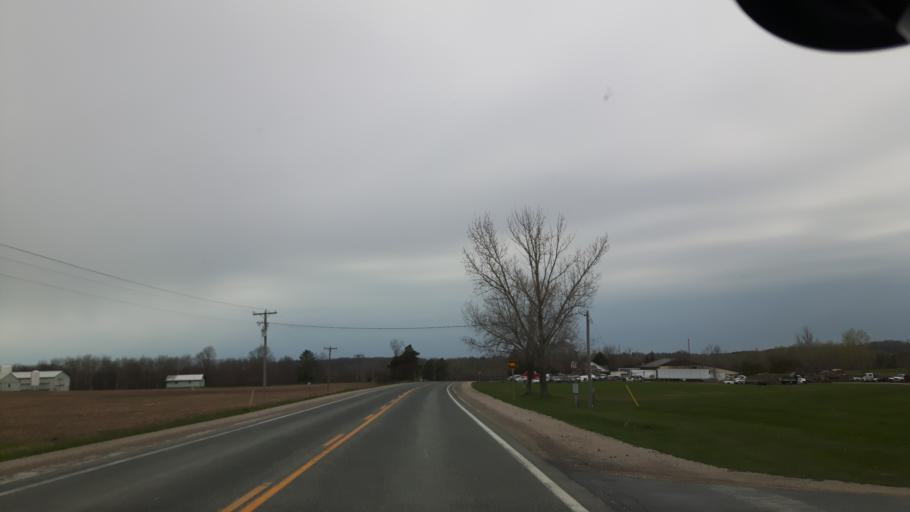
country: CA
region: Ontario
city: Bluewater
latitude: 43.6374
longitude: -81.5863
